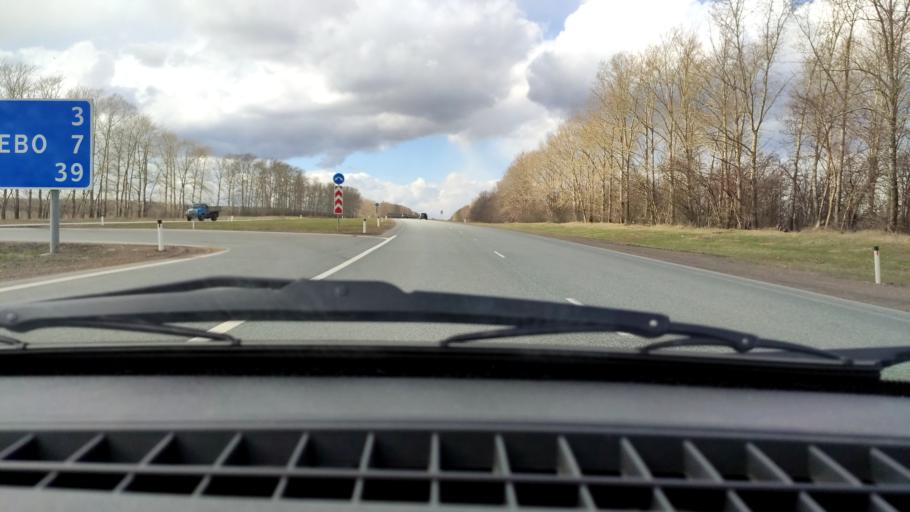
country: RU
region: Bashkortostan
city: Kushnarenkovo
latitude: 55.0299
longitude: 55.4639
